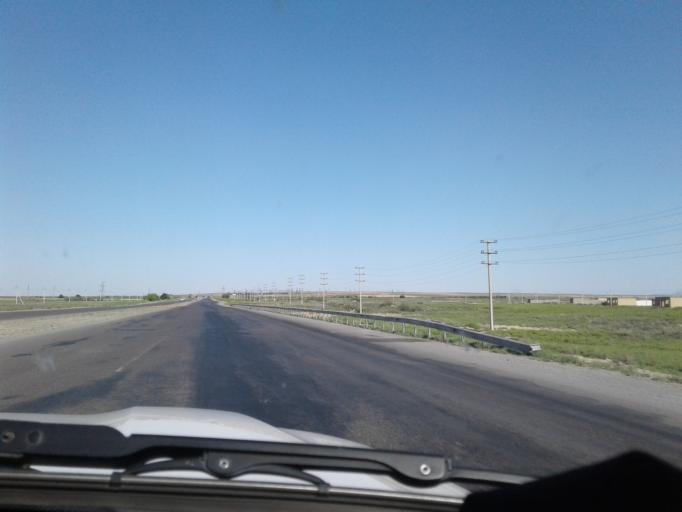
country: TM
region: Ahal
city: Kaka
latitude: 37.3572
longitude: 59.6385
